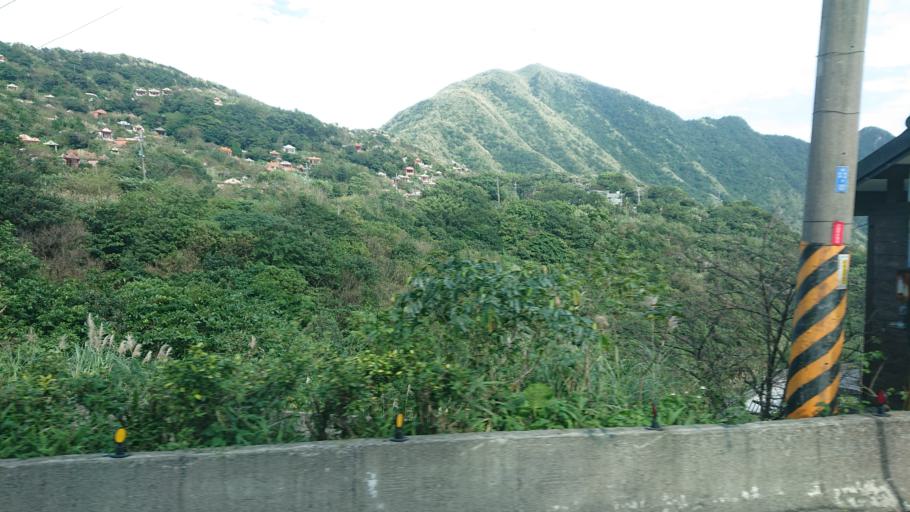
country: TW
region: Taiwan
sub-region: Keelung
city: Keelung
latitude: 25.1078
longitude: 121.8502
